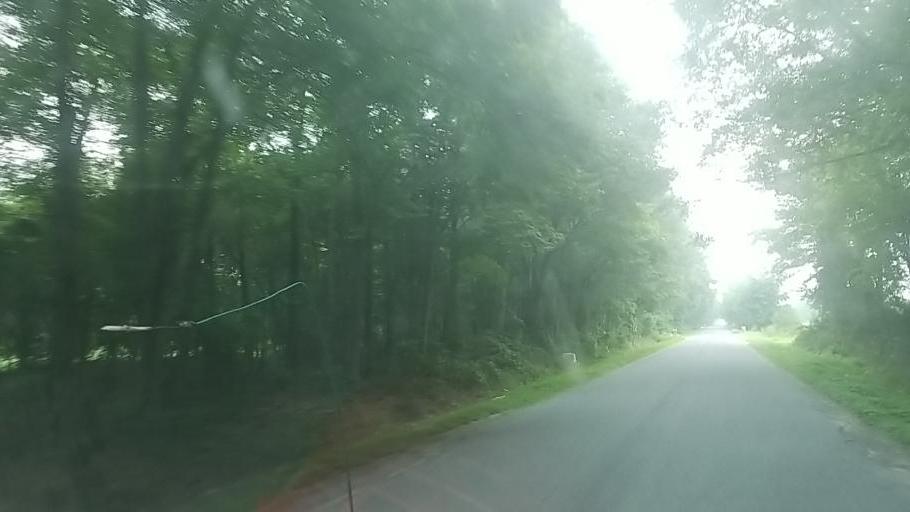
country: US
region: Maryland
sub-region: Wicomico County
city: Pittsville
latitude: 38.4521
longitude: -75.3856
